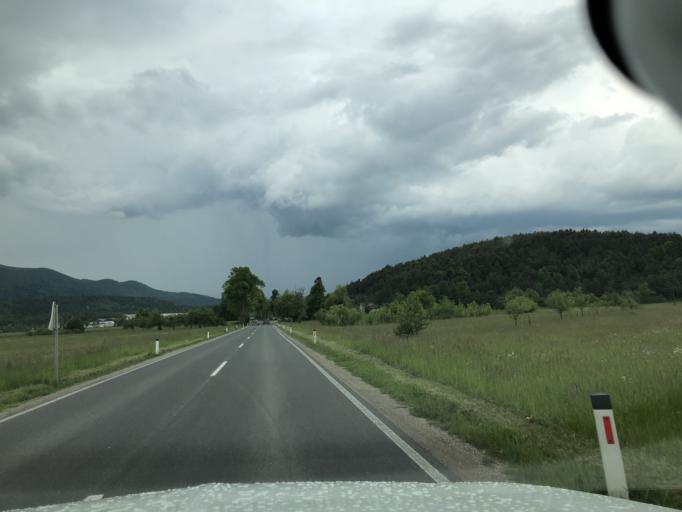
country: SI
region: Cerknica
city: Cerknica
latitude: 45.7956
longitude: 14.3505
